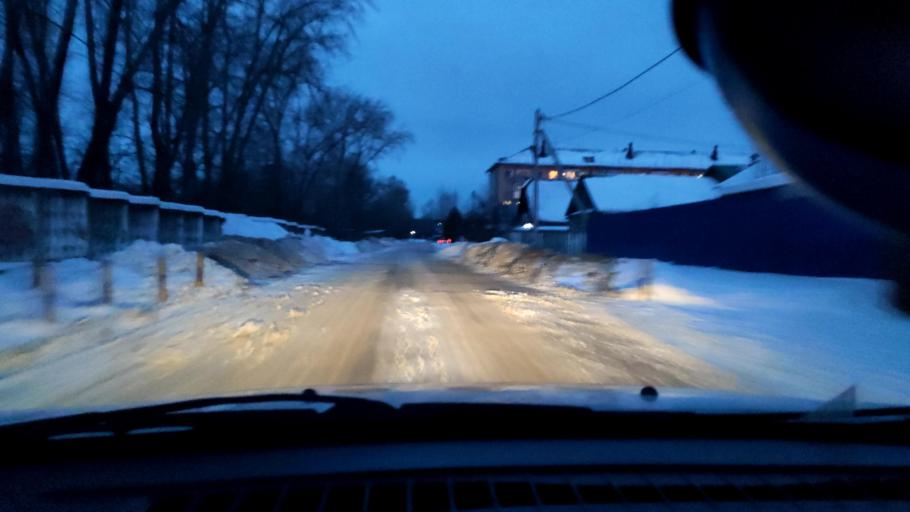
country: RU
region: Perm
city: Overyata
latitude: 58.0040
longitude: 55.9204
